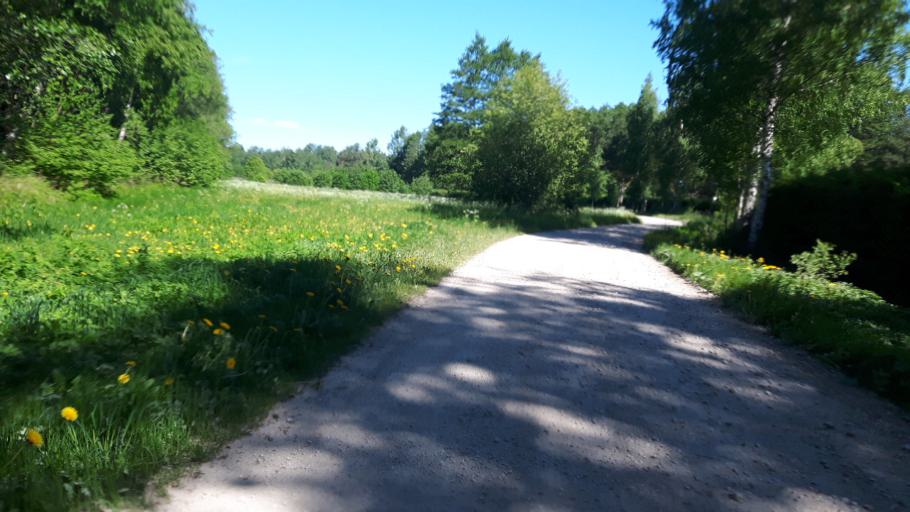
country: EE
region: Harju
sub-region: Loksa linn
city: Loksa
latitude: 59.5651
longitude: 25.8565
